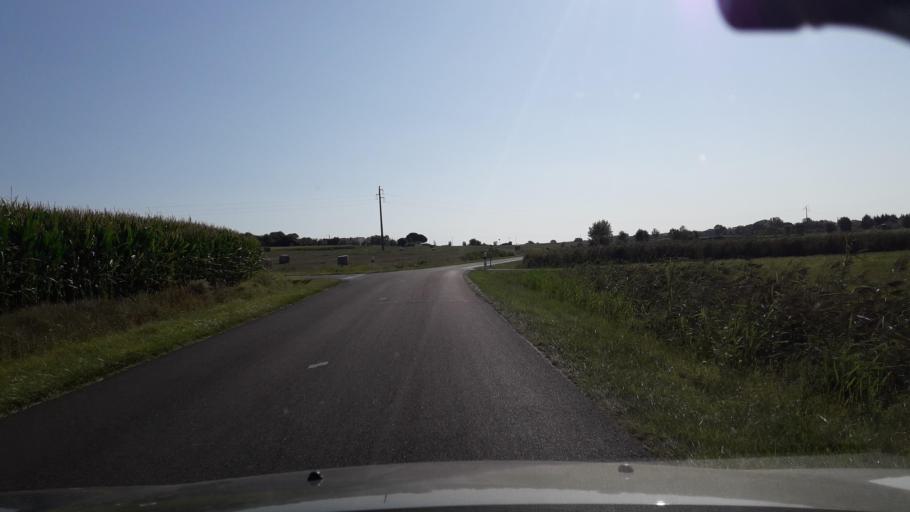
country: FR
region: Poitou-Charentes
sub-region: Departement de la Charente-Maritime
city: Etaules
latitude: 45.7107
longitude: -1.1184
